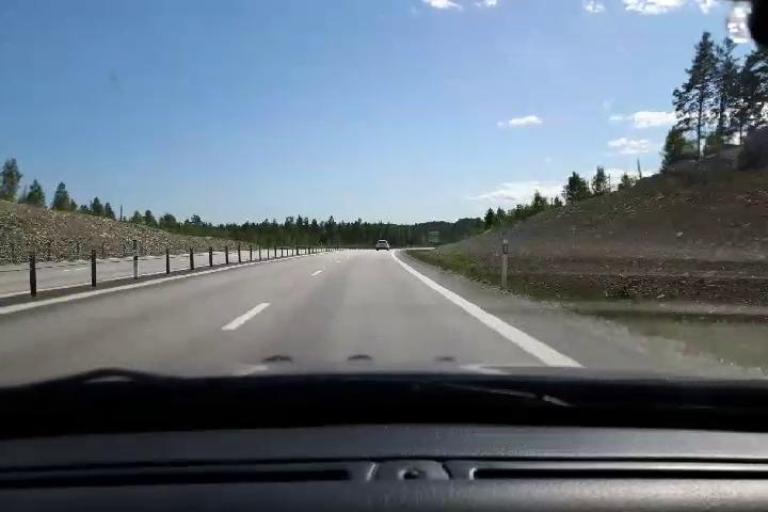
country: SE
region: Gaevleborg
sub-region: Hudiksvalls Kommun
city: Iggesund
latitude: 61.6932
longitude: 17.0569
